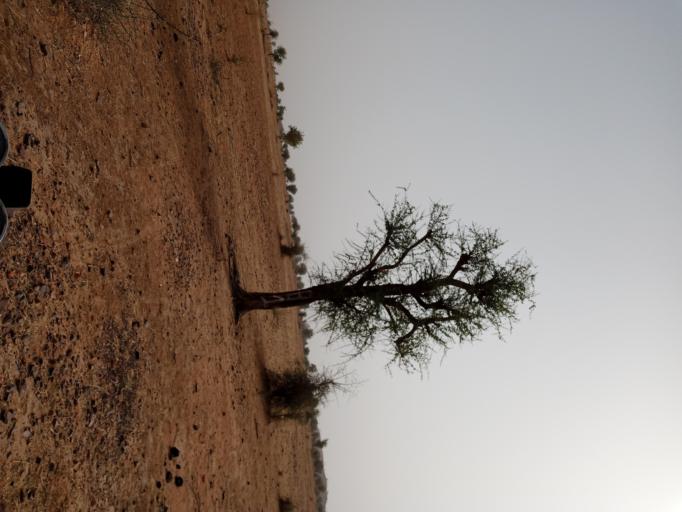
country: BF
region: Est
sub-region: Gnagna Province
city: Bogande
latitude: 13.2796
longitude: -0.1352
